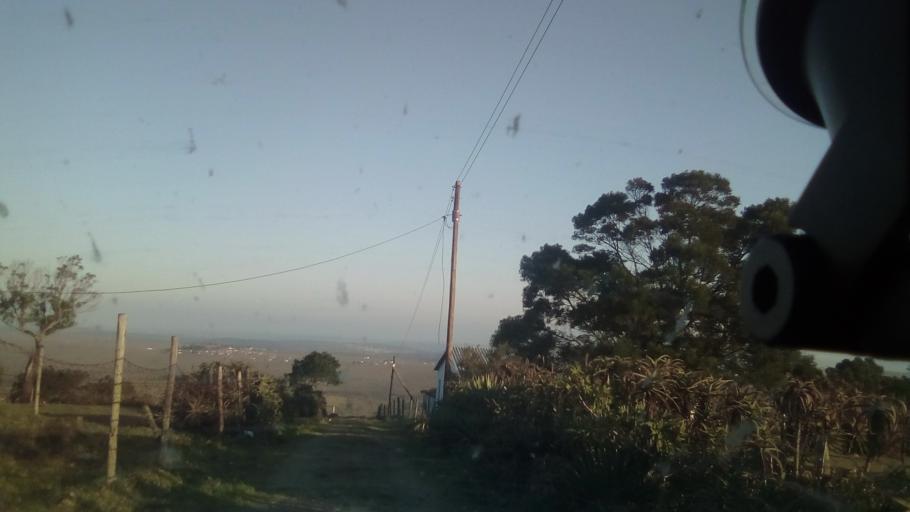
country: ZA
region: Eastern Cape
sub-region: Buffalo City Metropolitan Municipality
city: Bhisho
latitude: -32.9731
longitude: 27.2936
